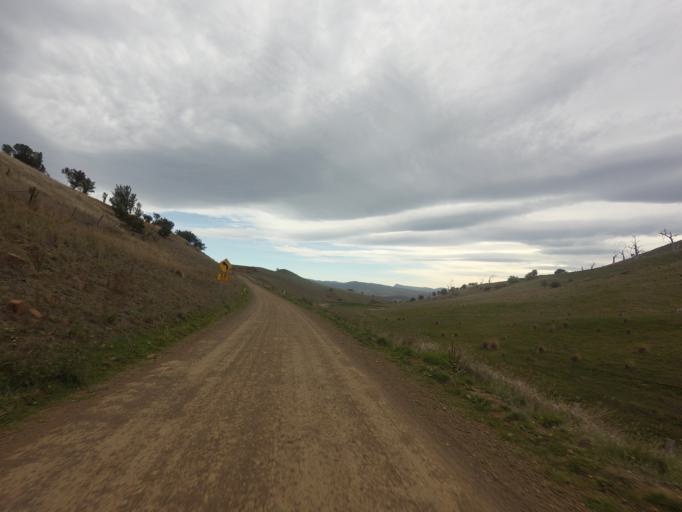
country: AU
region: Tasmania
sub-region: Derwent Valley
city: New Norfolk
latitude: -42.4503
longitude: 146.7726
